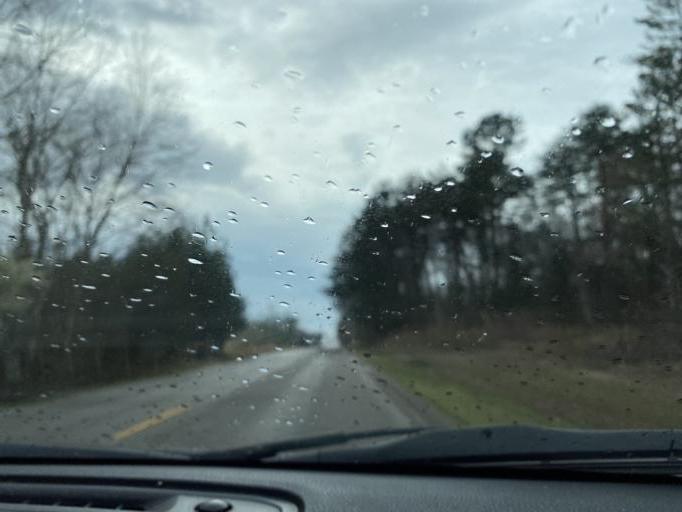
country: US
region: South Carolina
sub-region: Spartanburg County
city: Cowpens
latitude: 35.0164
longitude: -81.7602
